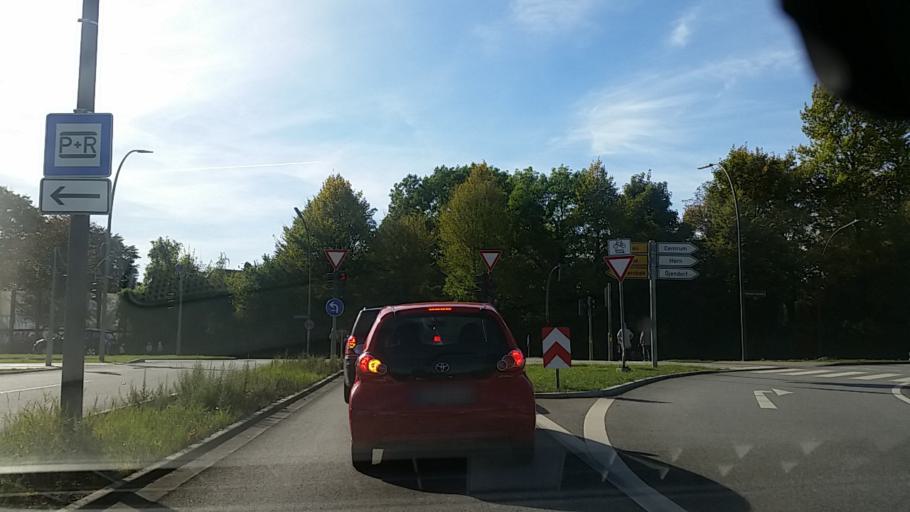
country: DE
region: Schleswig-Holstein
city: Oststeinbek
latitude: 53.5454
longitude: 10.1451
